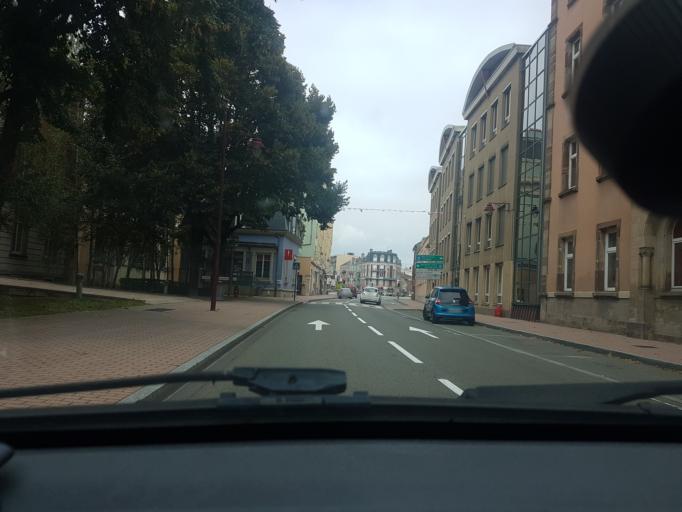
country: FR
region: Franche-Comte
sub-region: Territoire de Belfort
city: Belfort
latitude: 47.6404
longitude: 6.8572
